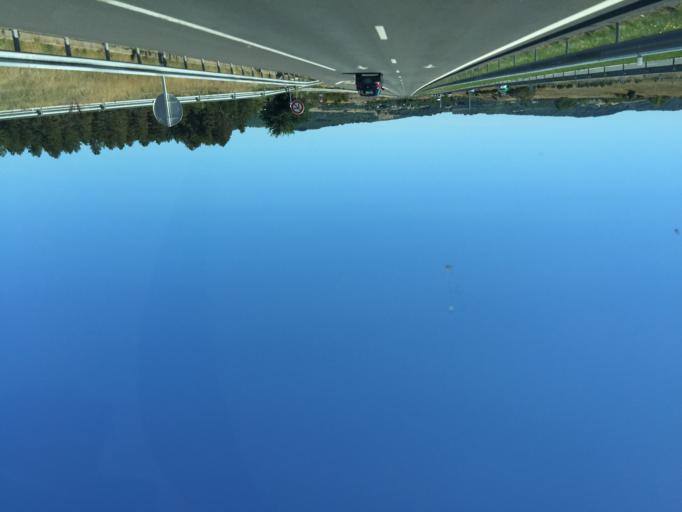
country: FR
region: Midi-Pyrenees
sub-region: Departement de l'Aveyron
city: La Cavalerie
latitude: 43.9509
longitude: 3.2165
